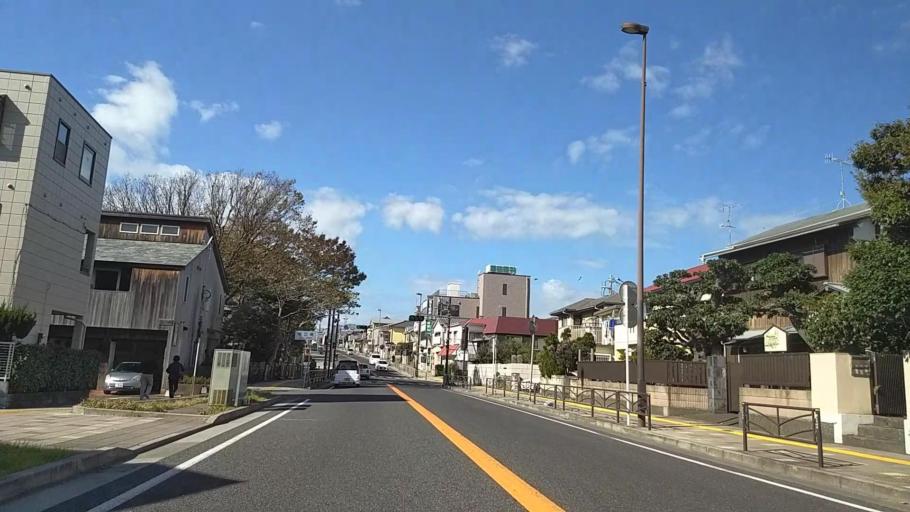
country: JP
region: Kanagawa
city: Oiso
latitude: 35.3075
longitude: 139.3121
